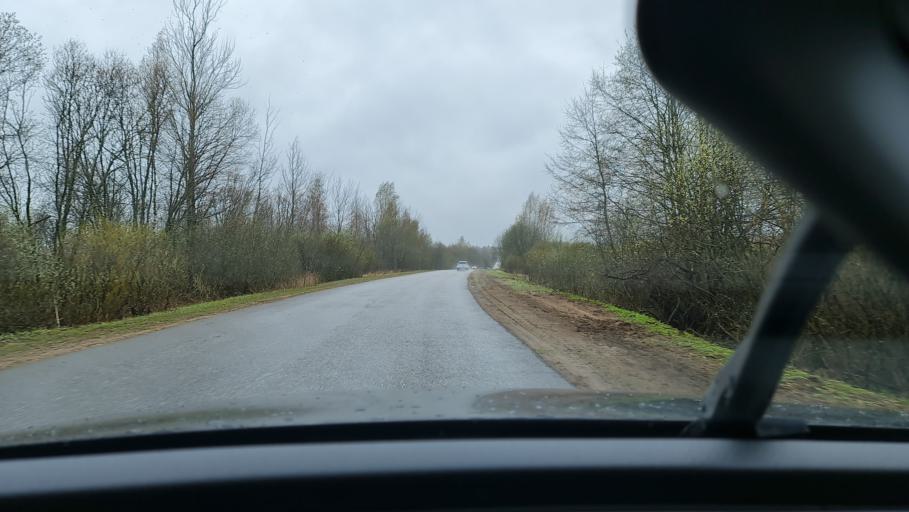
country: RU
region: Novgorod
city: Kresttsy
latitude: 57.9758
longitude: 32.7338
